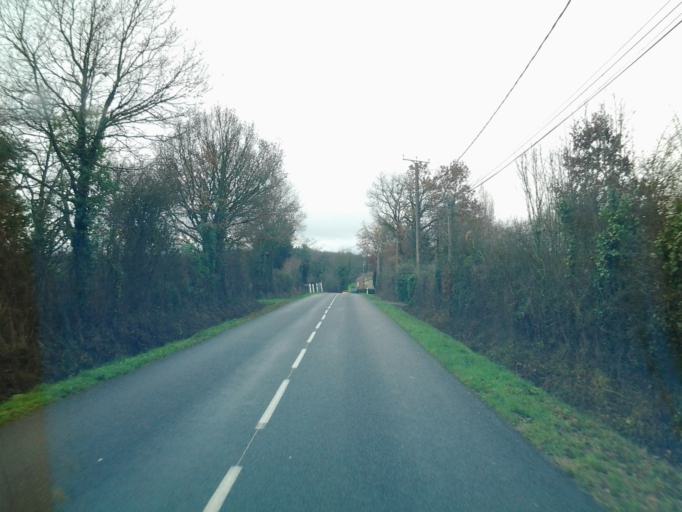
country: FR
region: Pays de la Loire
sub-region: Departement de la Vendee
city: La Roche-sur-Yon
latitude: 46.6726
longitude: -1.3859
